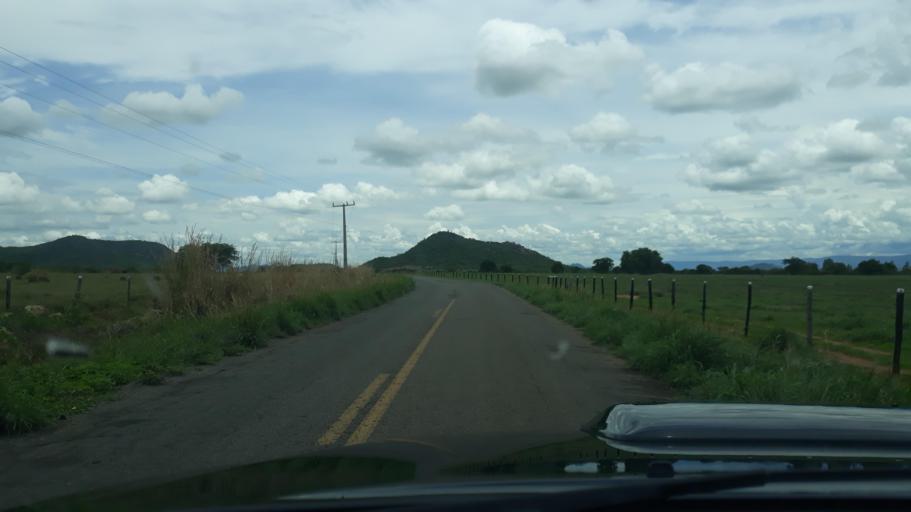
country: BR
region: Bahia
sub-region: Guanambi
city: Guanambi
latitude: -14.0994
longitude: -42.8715
